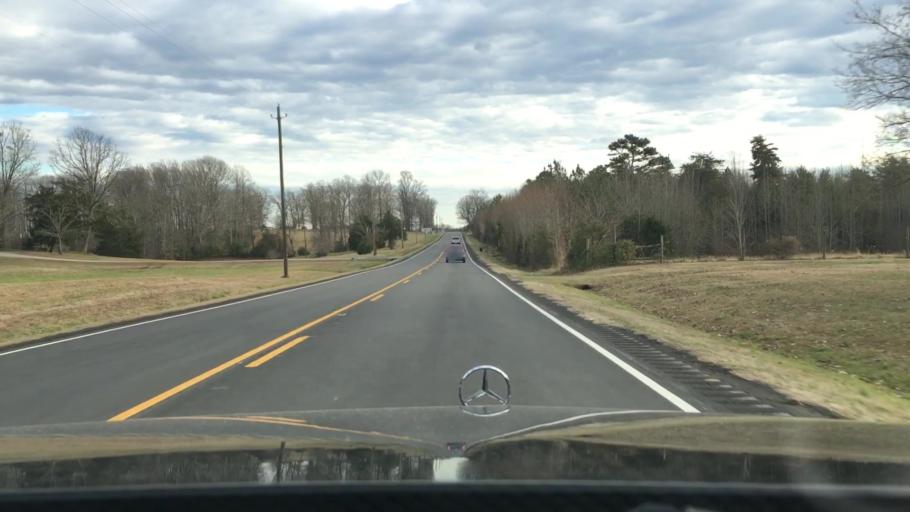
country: US
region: North Carolina
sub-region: Caswell County
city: Yanceyville
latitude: 36.3786
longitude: -79.2631
